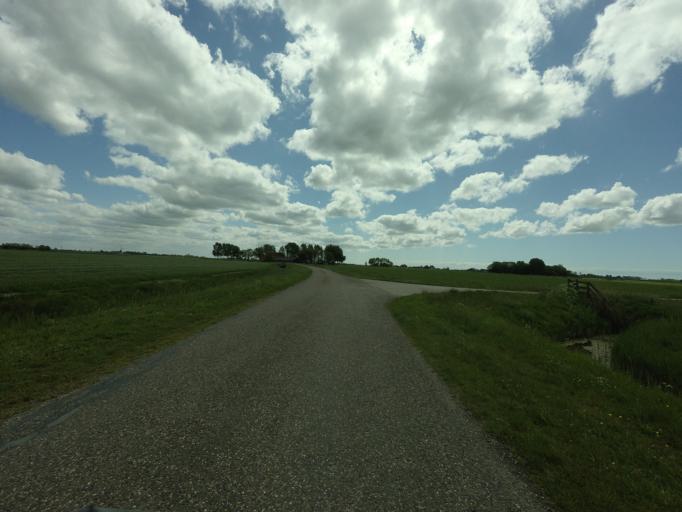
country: NL
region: Friesland
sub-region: Gemeente Franekeradeel
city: Tzum
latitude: 53.1393
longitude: 5.5580
